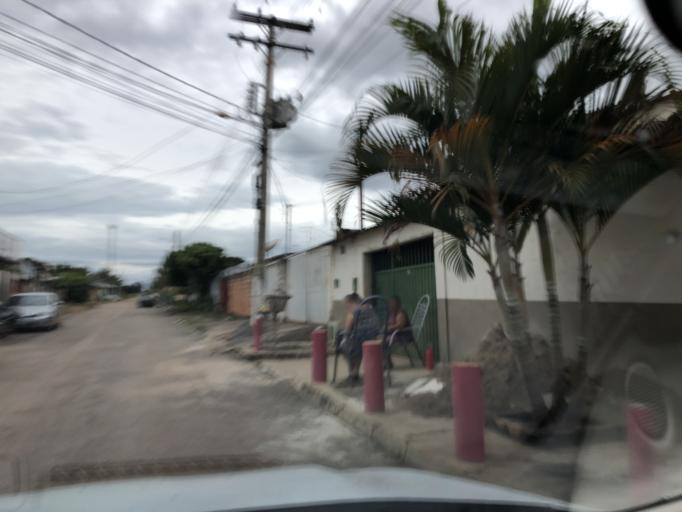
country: BR
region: Goias
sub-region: Luziania
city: Luziania
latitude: -16.1527
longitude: -47.9436
